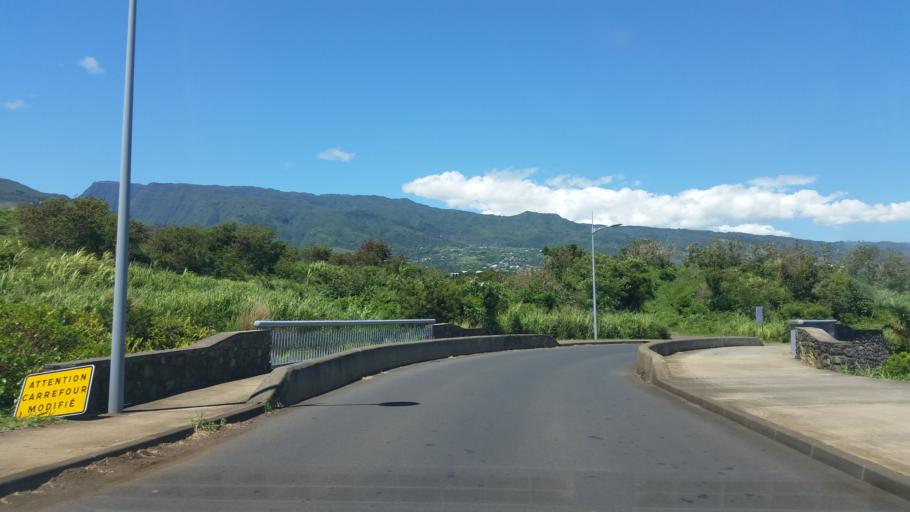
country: RE
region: Reunion
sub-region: Reunion
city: Sainte-Marie
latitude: -20.9178
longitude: 55.5272
